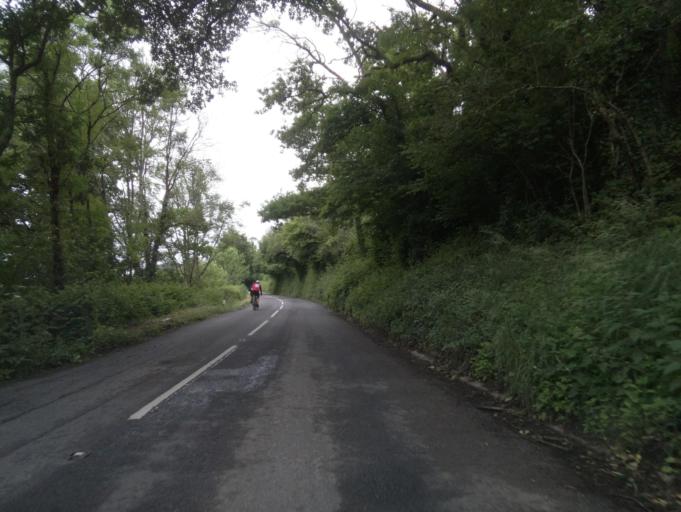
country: GB
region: England
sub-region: Devon
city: Chudleigh
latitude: 50.6621
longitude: -3.6428
